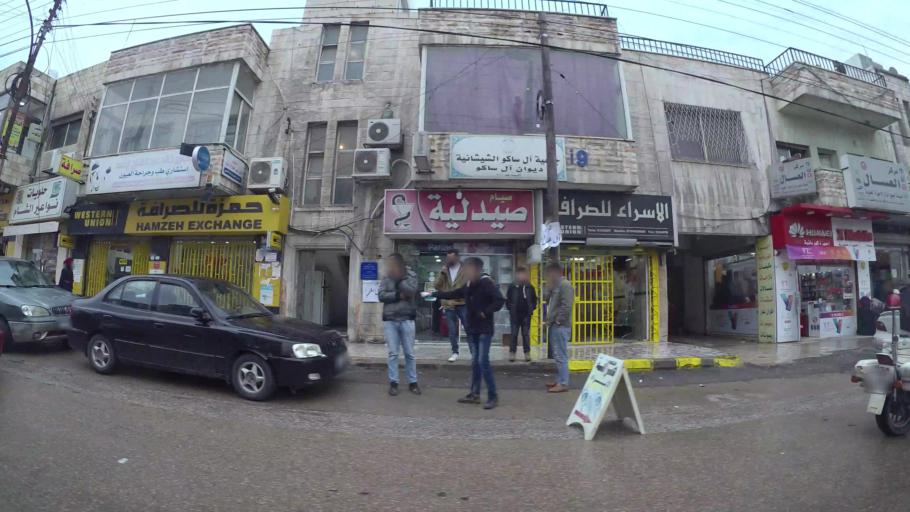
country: JO
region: Amman
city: Al Jubayhah
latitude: 32.0227
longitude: 35.8421
